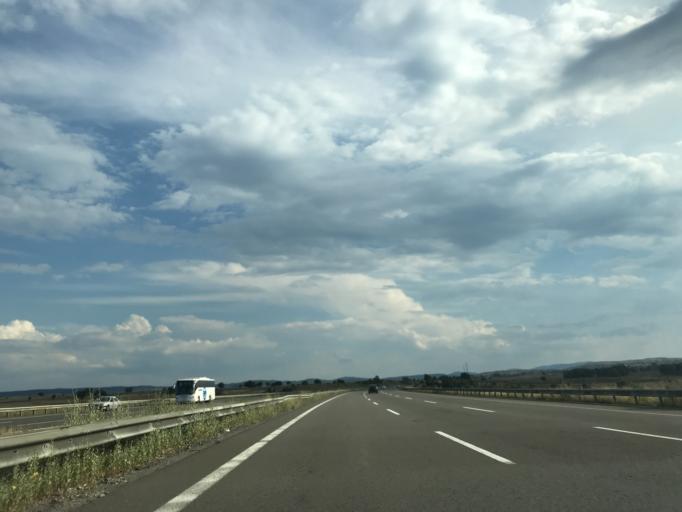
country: TR
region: Bolu
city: Gerede
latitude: 40.7115
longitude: 32.2229
